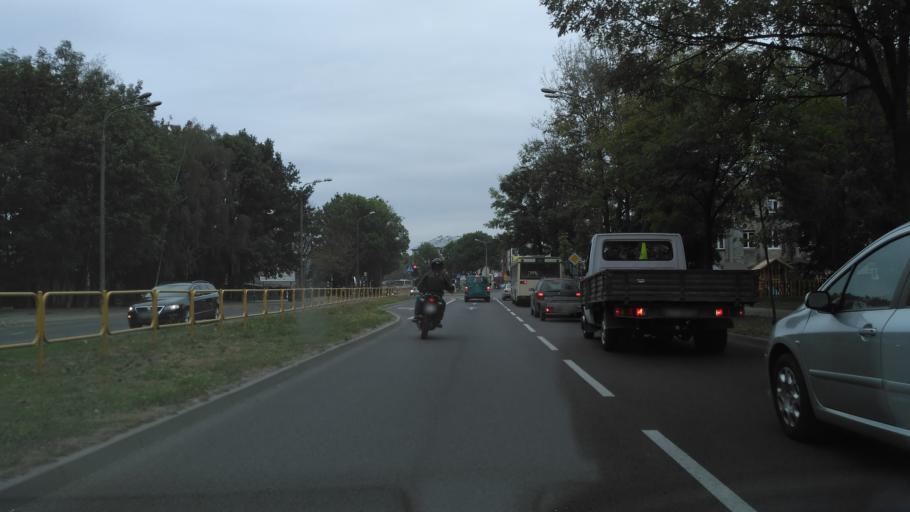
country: PL
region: Lublin Voivodeship
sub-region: Chelm
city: Chelm
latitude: 51.1331
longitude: 23.4644
